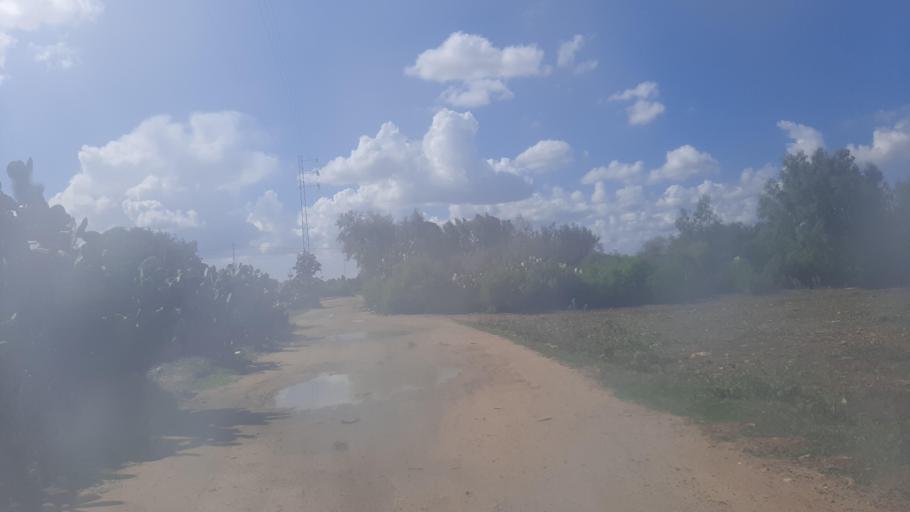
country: TN
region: Nabul
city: Korba
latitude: 36.6249
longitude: 10.8601
